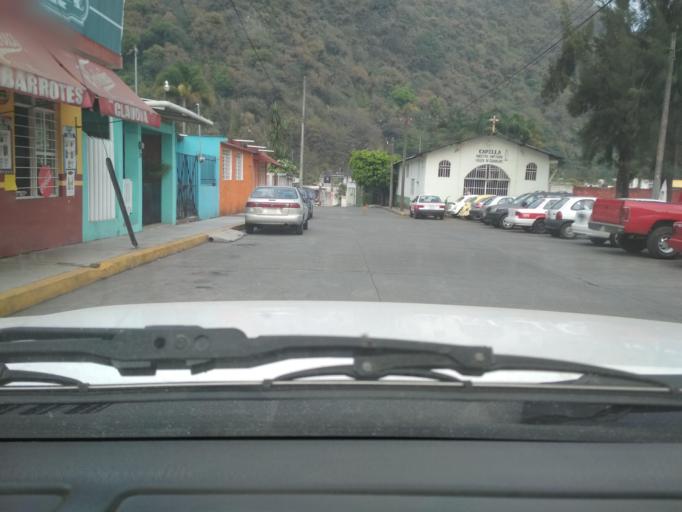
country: MX
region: Veracruz
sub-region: Mariano Escobedo
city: Palmira
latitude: 18.8739
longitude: -97.1004
